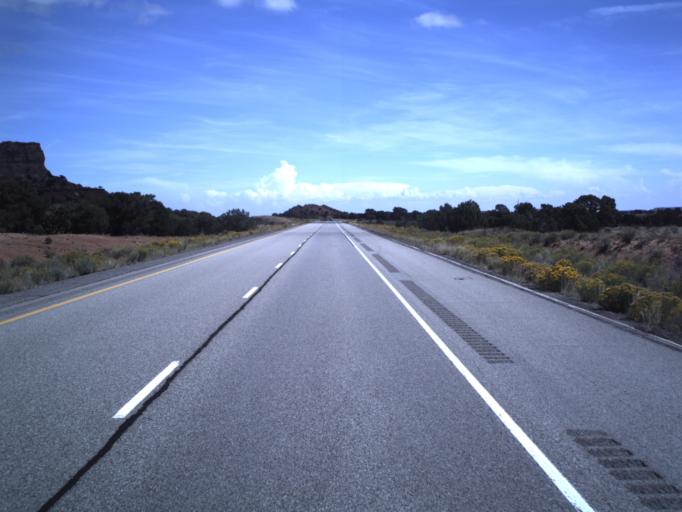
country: US
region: Utah
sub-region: Emery County
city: Castle Dale
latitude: 38.8697
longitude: -110.7240
